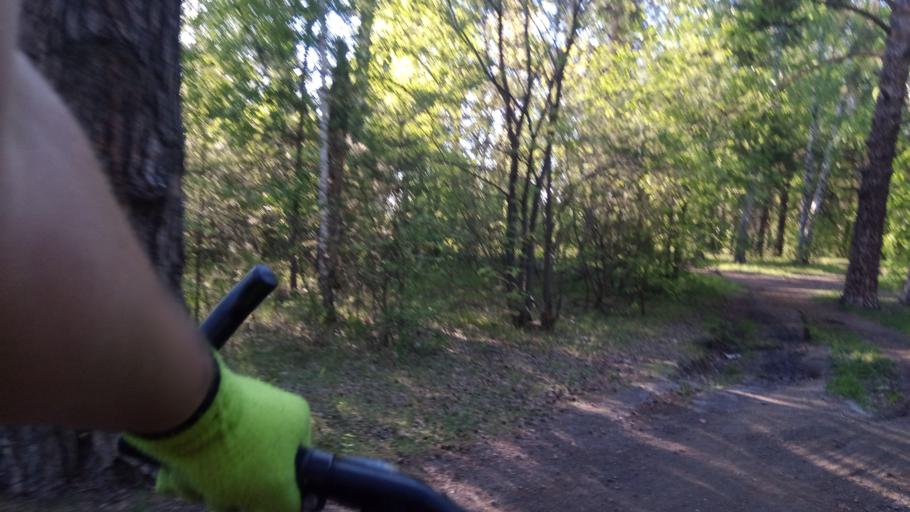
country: RU
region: Chelyabinsk
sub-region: Gorod Chelyabinsk
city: Chelyabinsk
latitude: 55.1408
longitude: 61.3312
